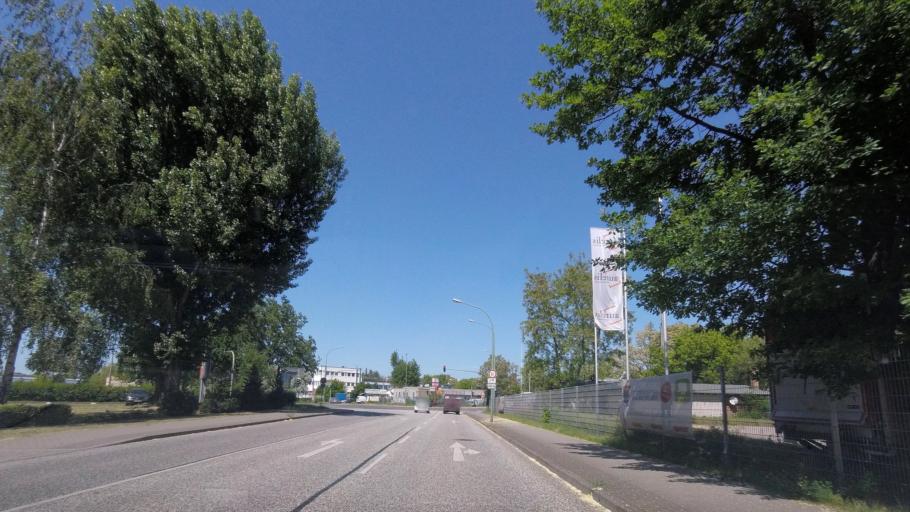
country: DE
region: Brandenburg
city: Potsdam
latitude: 52.3596
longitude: 13.1127
